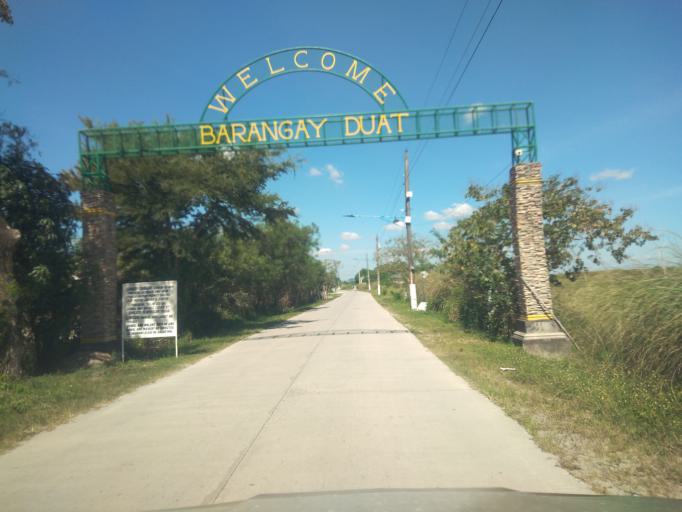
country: PH
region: Central Luzon
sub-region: Province of Pampanga
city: San Basilio
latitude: 15.0360
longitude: 120.6211
